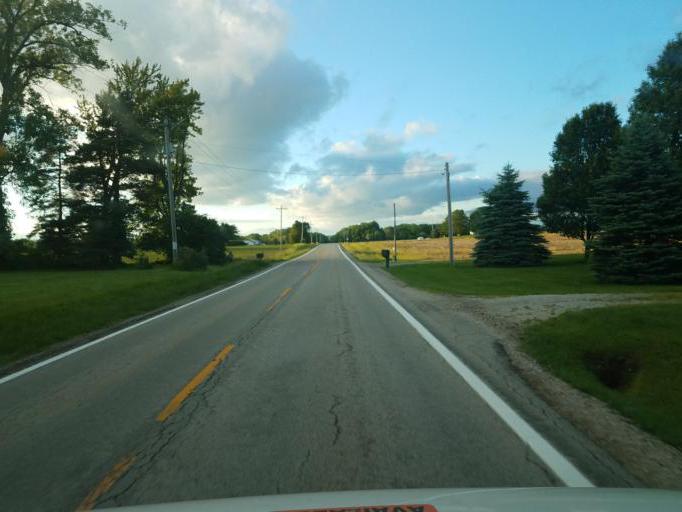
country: US
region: Ohio
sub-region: Knox County
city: Centerburg
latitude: 40.4317
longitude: -82.6987
